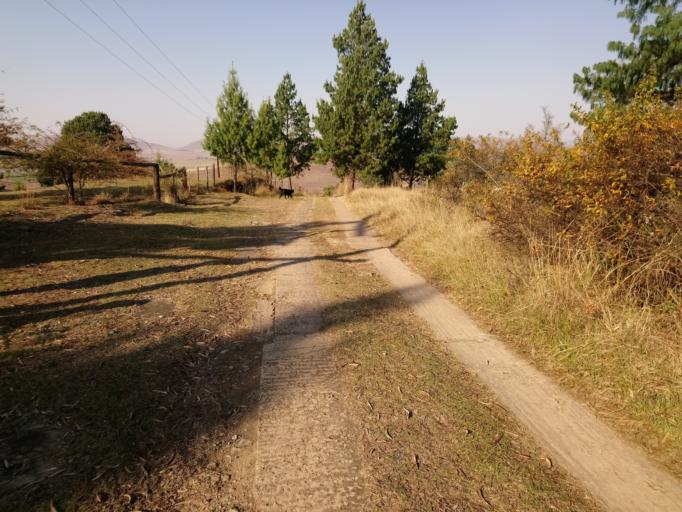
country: ZA
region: KwaZulu-Natal
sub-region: uMgungundlovu District Municipality
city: Mooirivier
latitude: -29.3340
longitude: 29.9197
